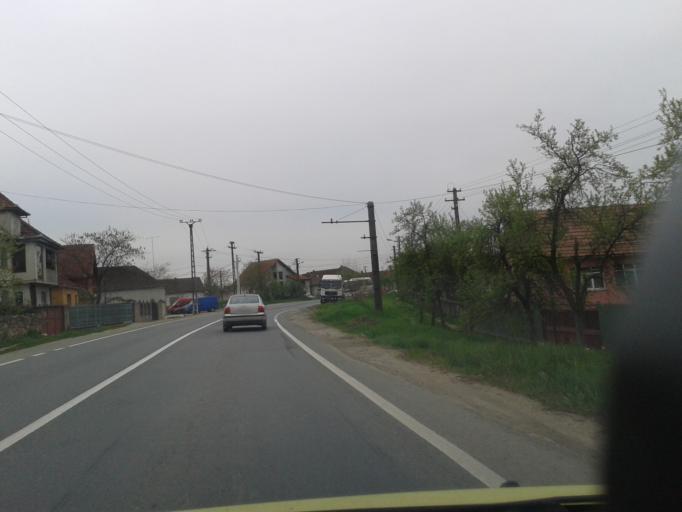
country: RO
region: Arad
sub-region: Oras Lipova
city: Radna
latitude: 46.0972
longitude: 21.6775
